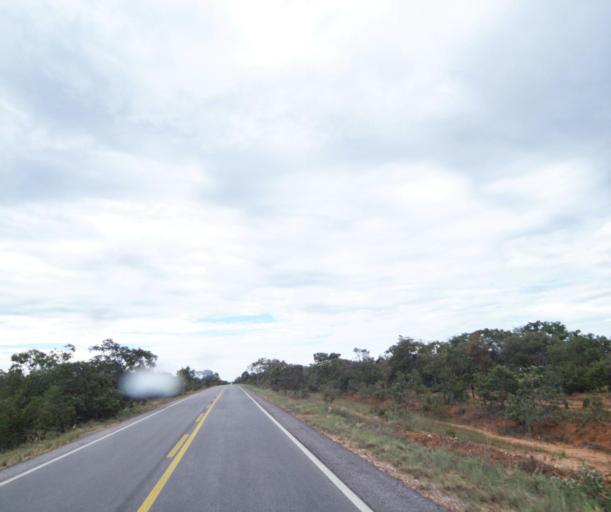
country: BR
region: Bahia
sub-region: Sao Felix Do Coribe
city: Santa Maria da Vitoria
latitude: -13.9663
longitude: -44.4460
